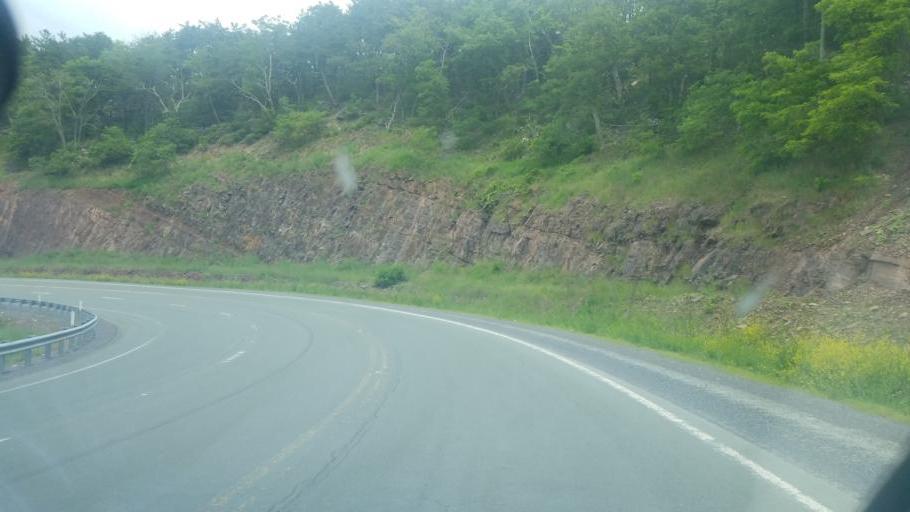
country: US
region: West Virginia
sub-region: Pendleton County
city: Franklin
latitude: 38.5902
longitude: -79.1697
